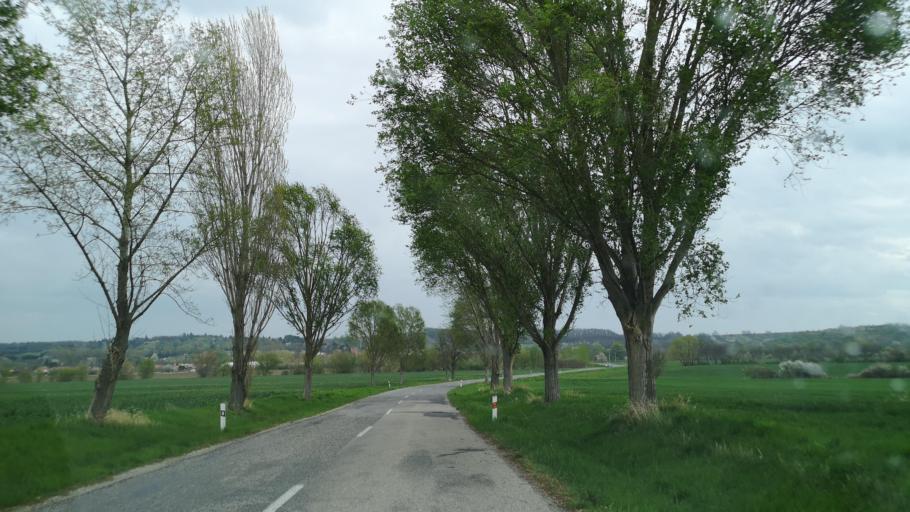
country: SK
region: Nitriansky
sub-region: Okres Nitra
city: Vrable
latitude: 48.3186
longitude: 18.3462
